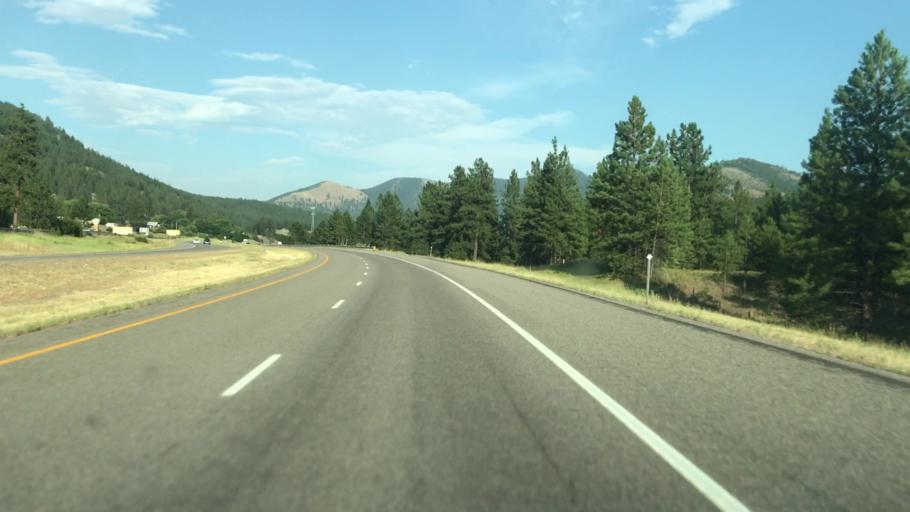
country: US
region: Montana
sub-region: Missoula County
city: Frenchtown
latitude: 47.0009
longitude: -114.4830
